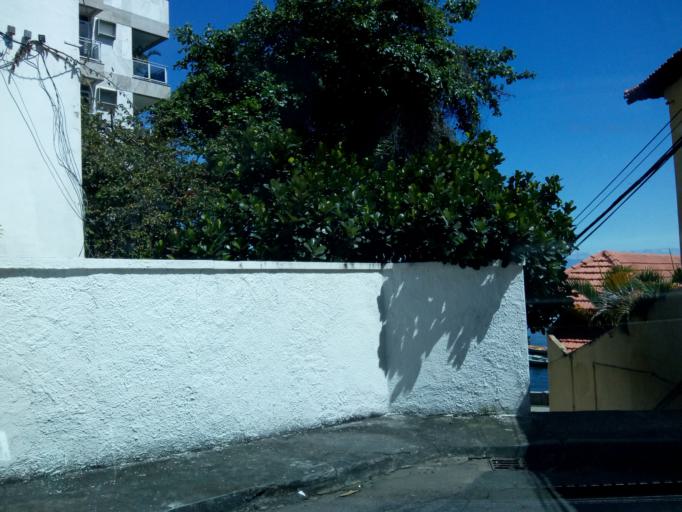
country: BR
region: Rio de Janeiro
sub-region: Rio De Janeiro
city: Rio de Janeiro
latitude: -22.9438
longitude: -43.1595
